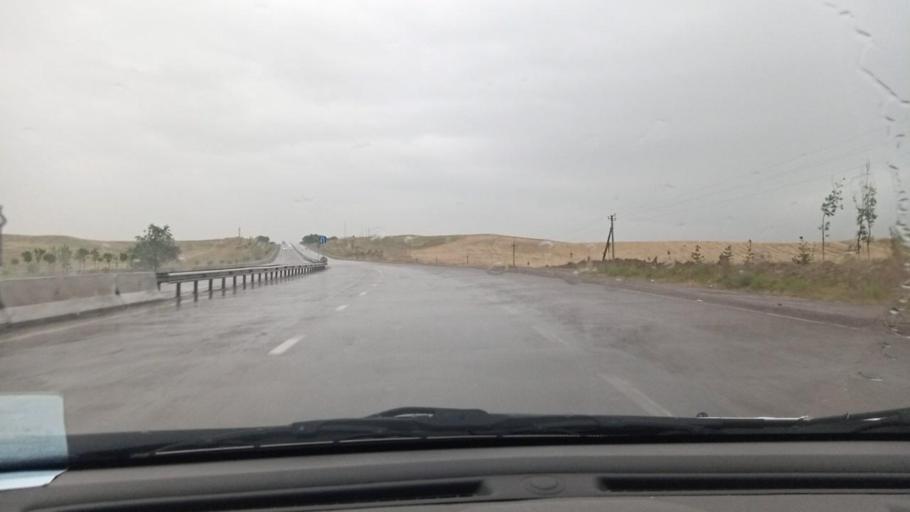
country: UZ
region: Toshkent
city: Ohangaron
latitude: 40.9691
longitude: 69.5485
